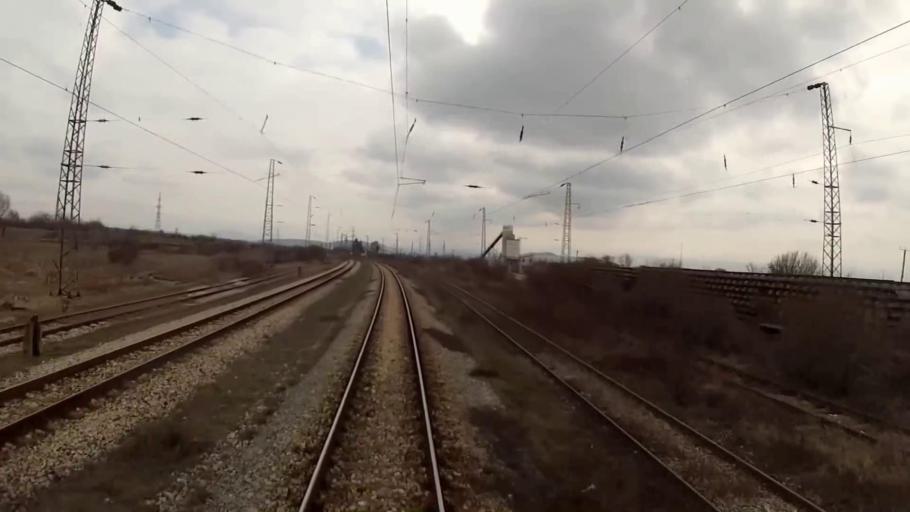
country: BG
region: Sofiya
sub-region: Obshtina Gorna Malina
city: Gorna Malina
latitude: 42.6994
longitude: 23.6527
